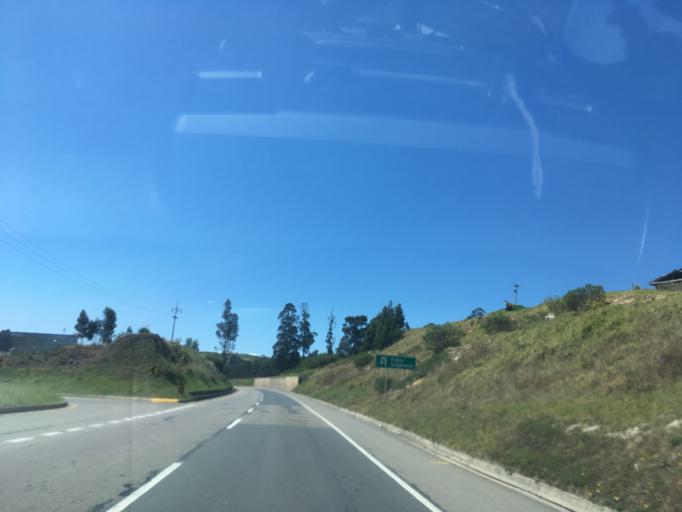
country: CO
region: Boyaca
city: Tuta
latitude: 5.7295
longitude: -73.2199
